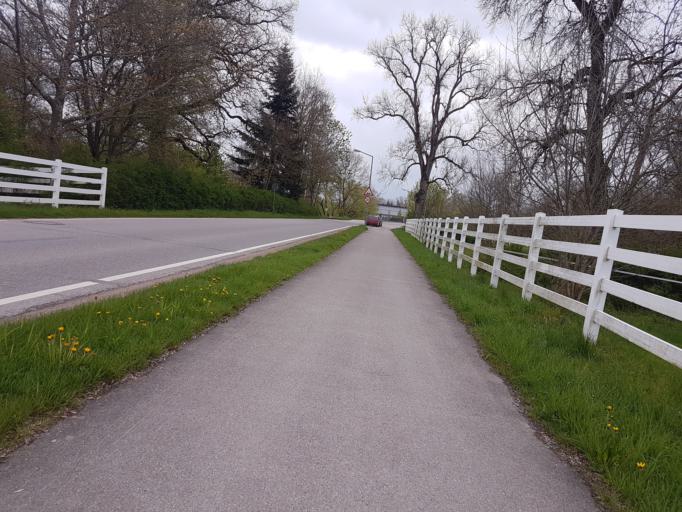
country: DE
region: Baden-Wuerttemberg
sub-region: Freiburg Region
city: Donaueschingen
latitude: 47.9518
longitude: 8.5119
